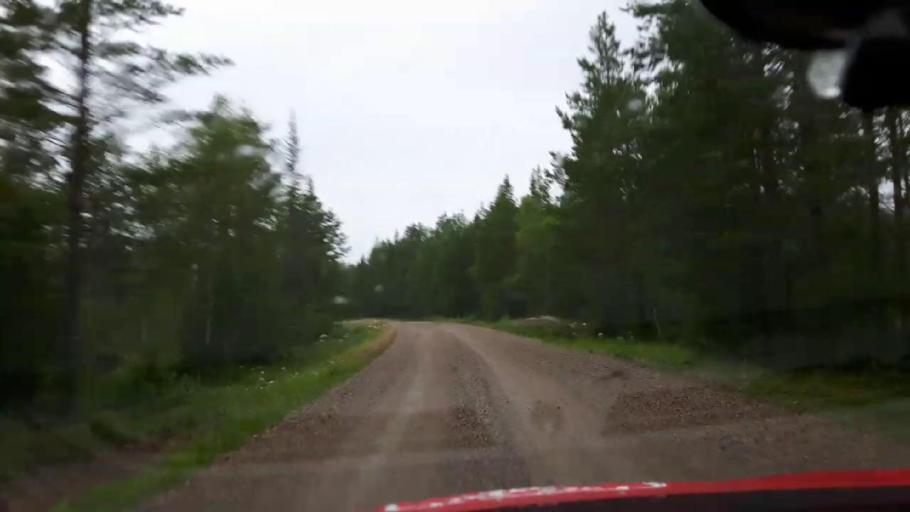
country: SE
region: Jaemtland
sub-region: OEstersunds Kommun
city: Brunflo
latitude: 62.8076
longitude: 14.8955
